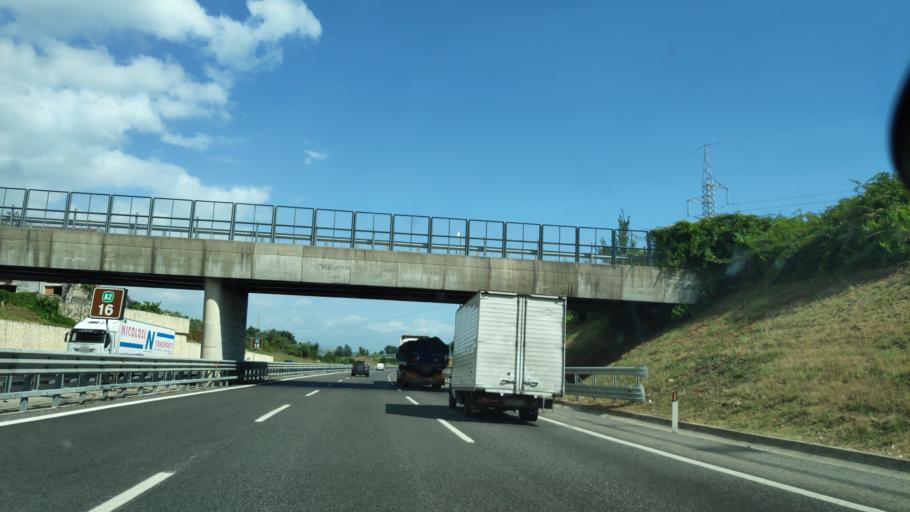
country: IT
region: Campania
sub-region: Provincia di Salerno
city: San Mango Piemonte
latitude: 40.6965
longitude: 14.8286
